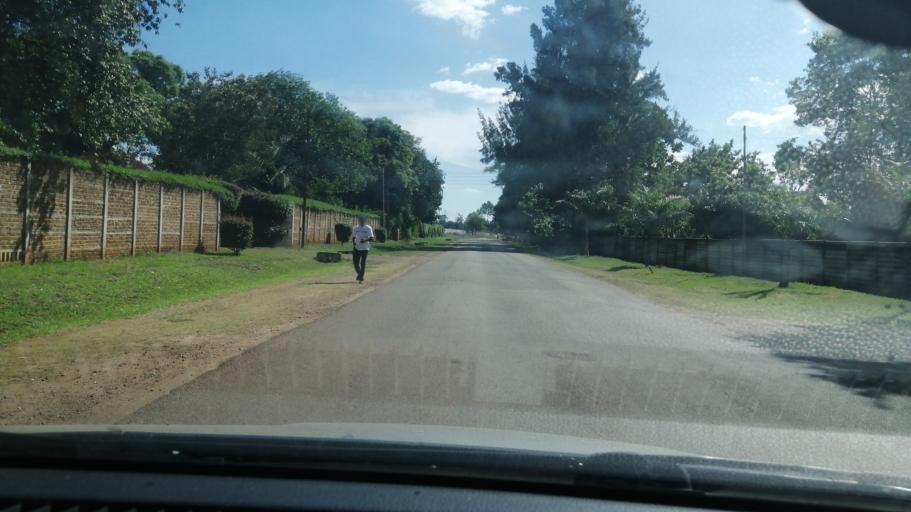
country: ZW
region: Harare
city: Harare
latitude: -17.7568
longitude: 31.0669
